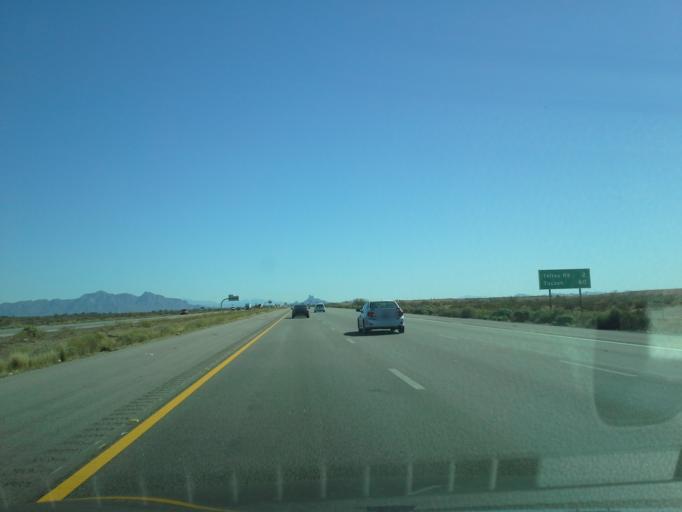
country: US
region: Arizona
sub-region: Pinal County
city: Arizona City
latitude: 32.7999
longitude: -111.6563
